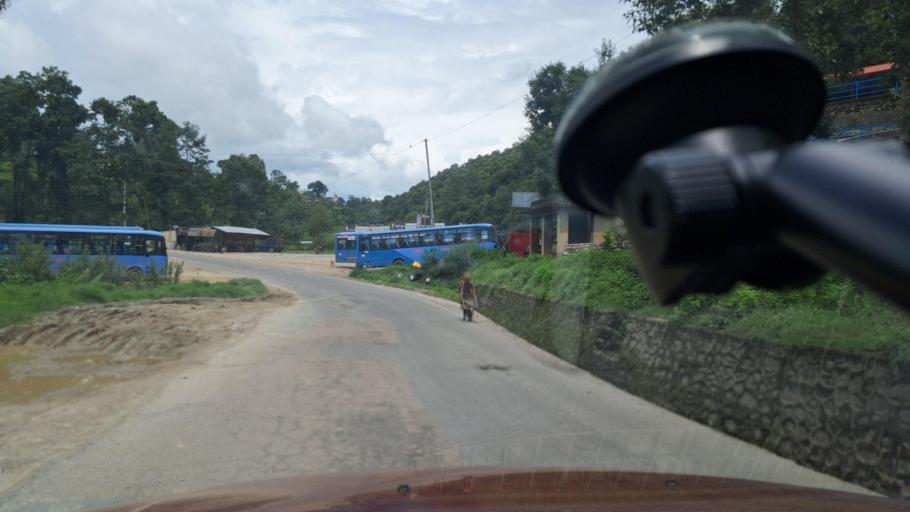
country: NP
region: Central Region
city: Banepa
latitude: 27.6121
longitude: 85.5532
